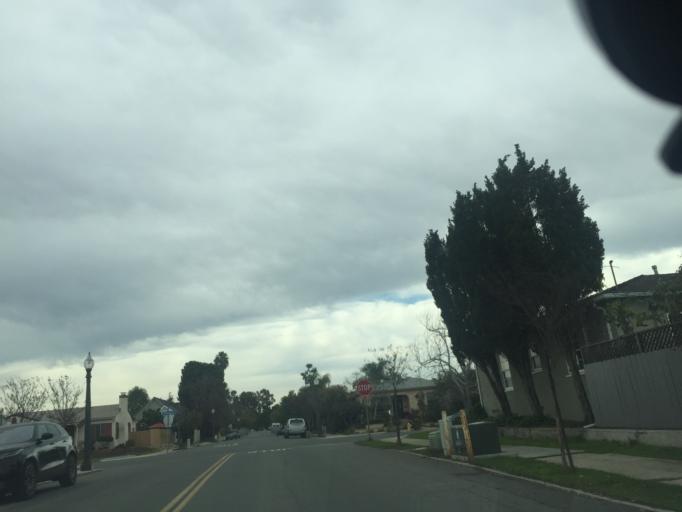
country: US
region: California
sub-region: San Diego County
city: Lemon Grove
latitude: 32.7629
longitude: -117.0883
